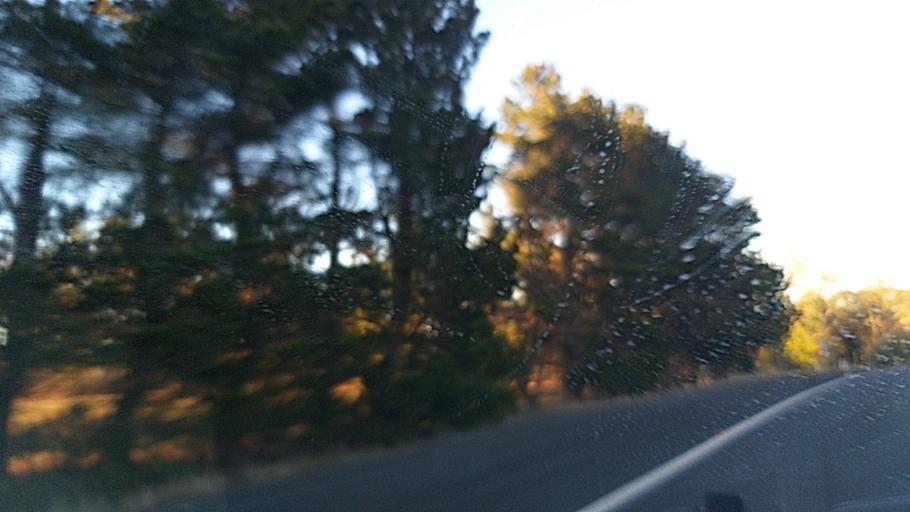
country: AU
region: New South Wales
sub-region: Goulburn Mulwaree
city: Goulburn
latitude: -34.8921
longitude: 149.5256
